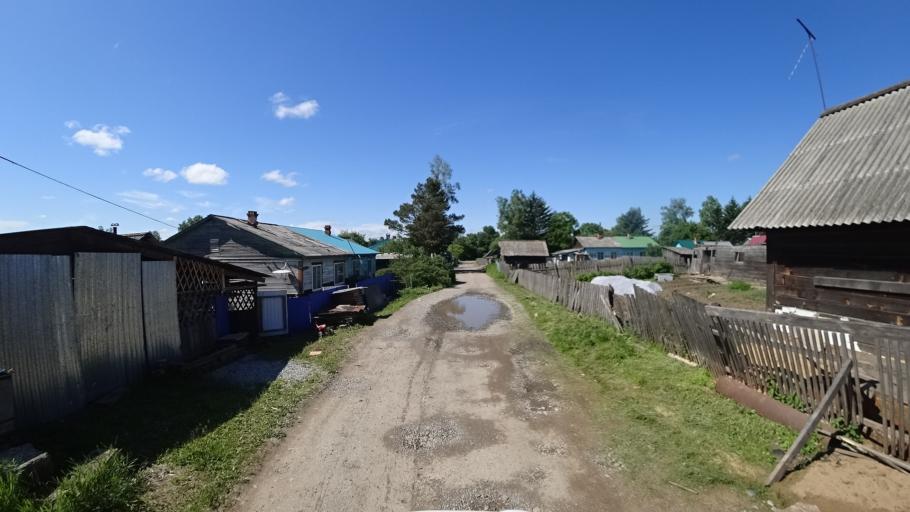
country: RU
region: Khabarovsk Krai
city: Khor
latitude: 47.8876
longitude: 135.0267
